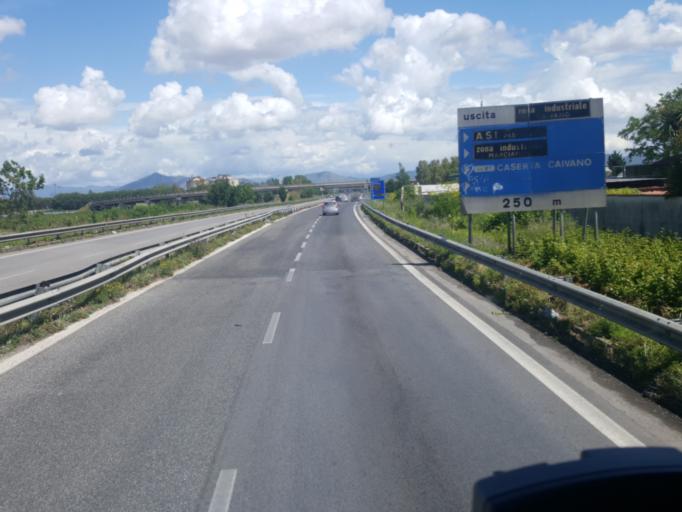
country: IT
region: Campania
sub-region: Provincia di Napoli
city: Pascarola
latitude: 40.9881
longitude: 14.2925
